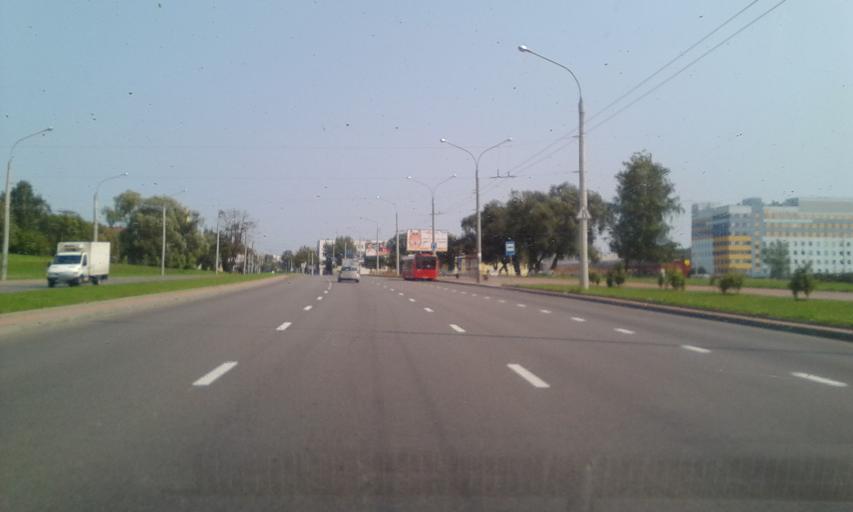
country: BY
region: Minsk
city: Novoye Medvezhino
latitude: 53.8712
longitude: 27.4973
